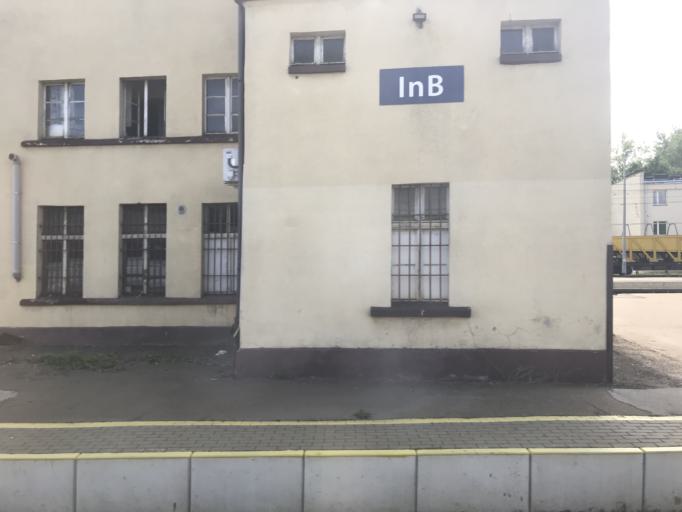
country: PL
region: Kujawsko-Pomorskie
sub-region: Powiat inowroclawski
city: Inowroclaw
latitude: 52.8045
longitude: 18.2433
